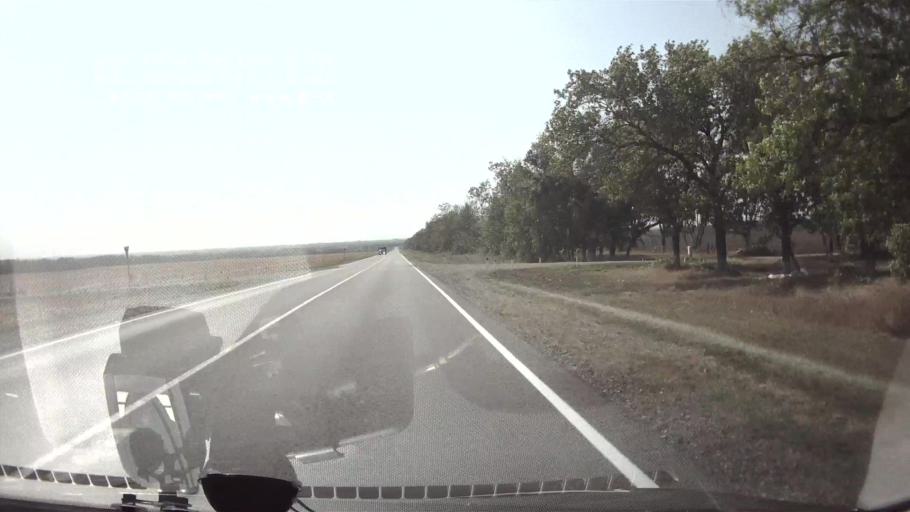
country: RU
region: Krasnodarskiy
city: Dmitriyevskaya
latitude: 45.7675
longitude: 40.7195
